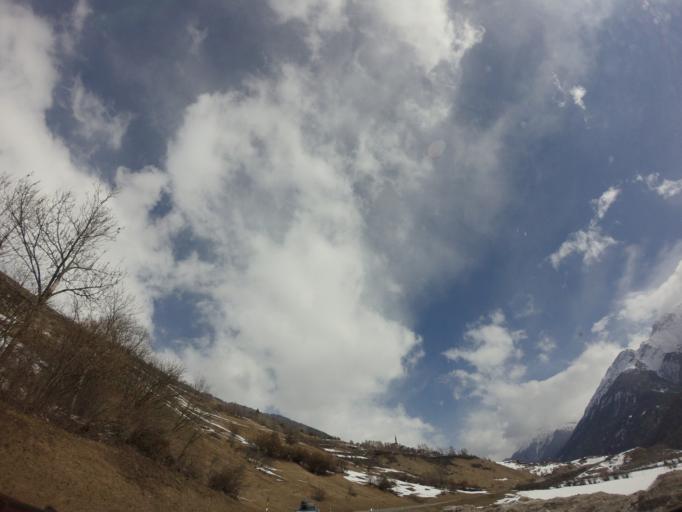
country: CH
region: Grisons
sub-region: Inn District
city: Scuol
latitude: 46.8088
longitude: 10.3256
